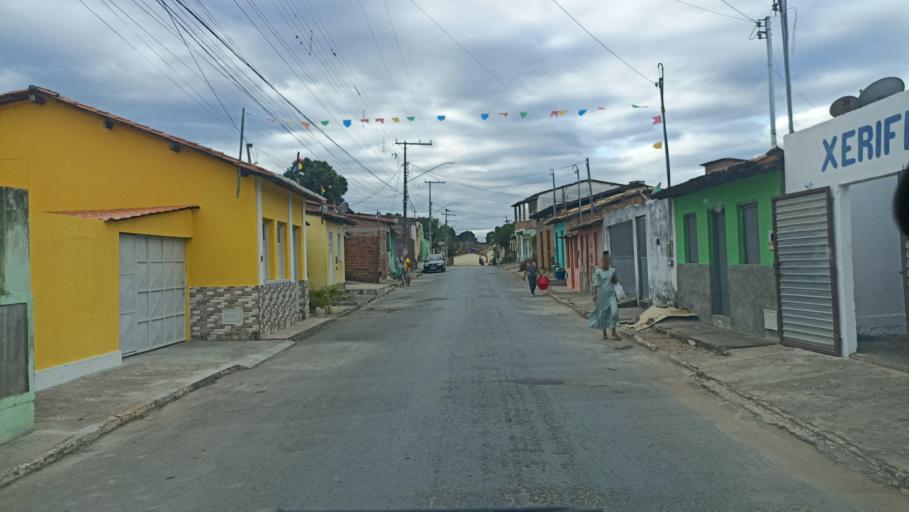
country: BR
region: Bahia
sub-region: Andarai
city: Vera Cruz
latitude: -12.8124
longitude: -41.3320
